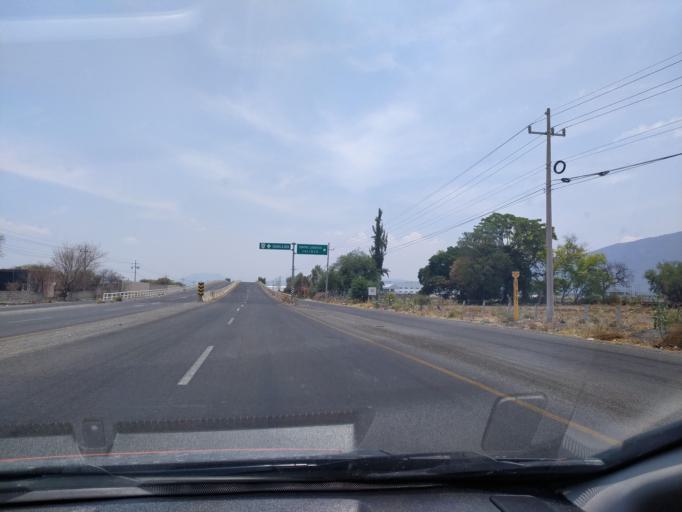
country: MX
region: Jalisco
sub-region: Acatlan de Juarez
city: Villa de los Ninos
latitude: 20.3384
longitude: -103.5909
